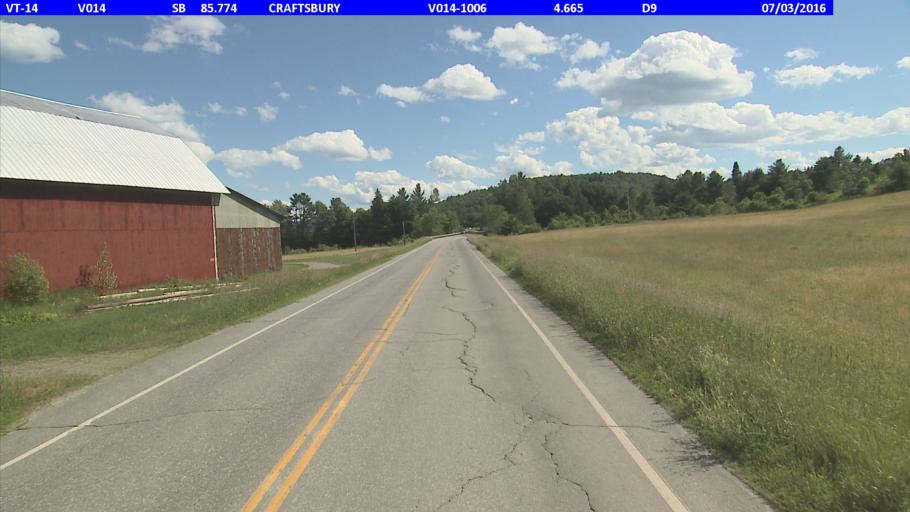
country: US
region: Vermont
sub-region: Caledonia County
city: Hardwick
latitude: 44.6577
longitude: -72.4039
